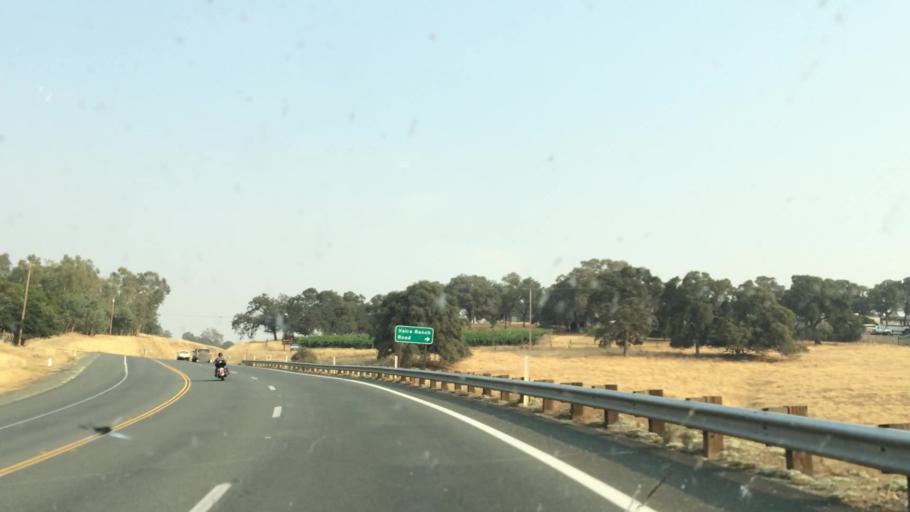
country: US
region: California
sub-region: Amador County
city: Plymouth
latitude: 38.4360
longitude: -120.8557
